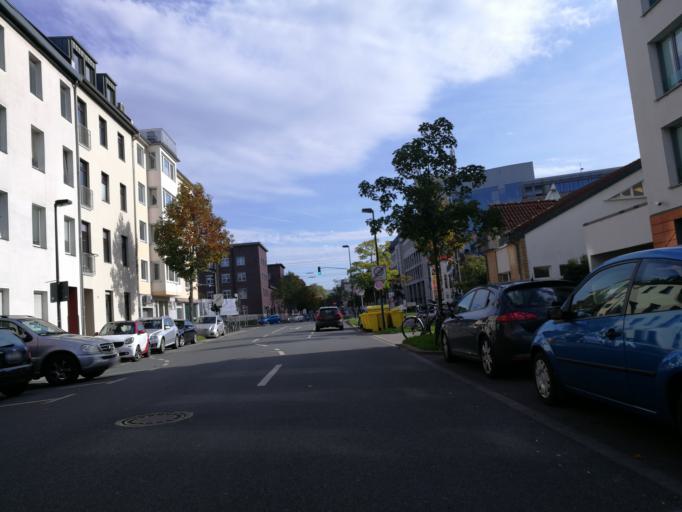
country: DE
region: North Rhine-Westphalia
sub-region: Regierungsbezirk Dusseldorf
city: Dusseldorf
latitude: 51.2166
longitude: 6.7640
